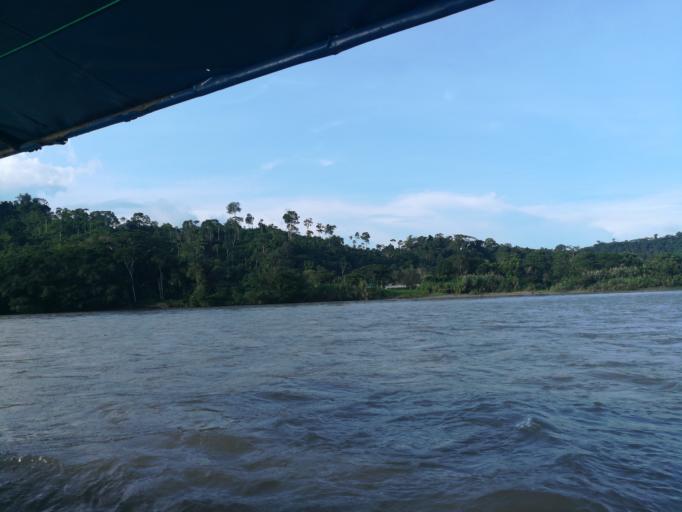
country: EC
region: Orellana
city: Boca Suno
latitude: -0.8807
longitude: -77.2882
